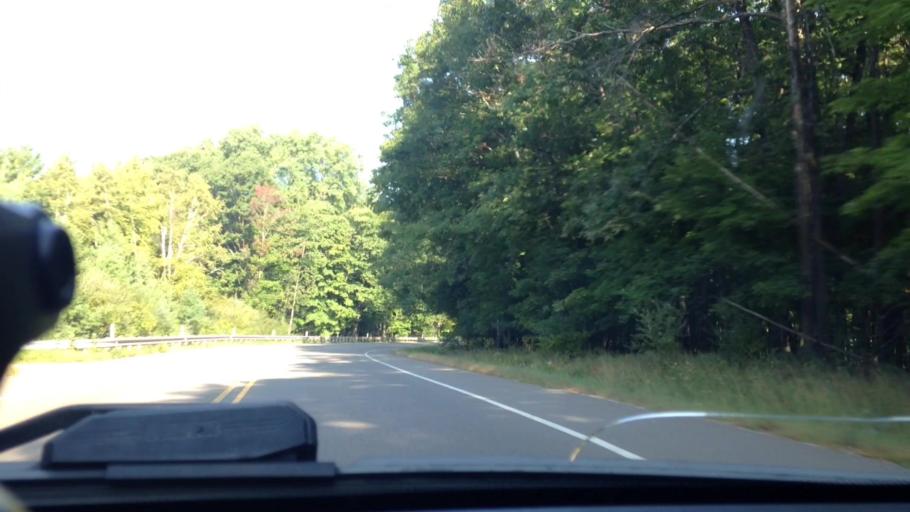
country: US
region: Michigan
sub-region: Dickinson County
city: Quinnesec
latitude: 45.8224
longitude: -87.9902
